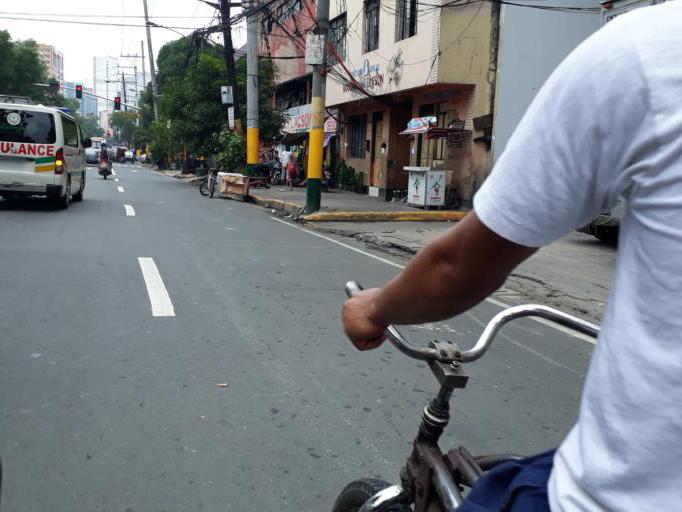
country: PH
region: Metro Manila
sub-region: City of Manila
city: Manila
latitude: 14.6121
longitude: 120.9762
